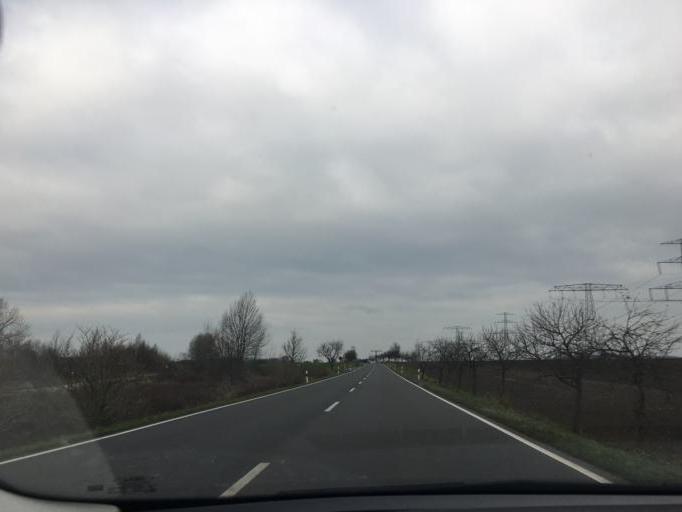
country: DE
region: Saxony
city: Kitzscher
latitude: 51.1404
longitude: 12.5448
